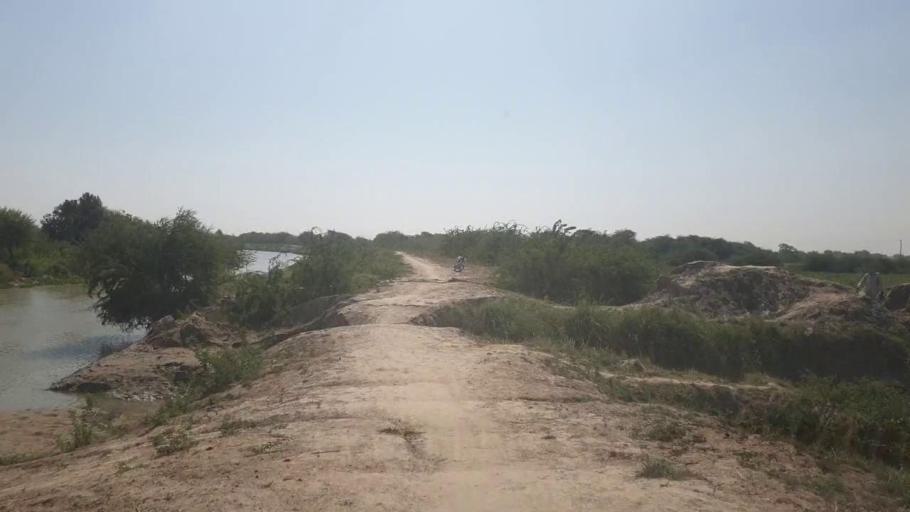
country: PK
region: Sindh
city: Talhar
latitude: 24.8044
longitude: 68.7921
